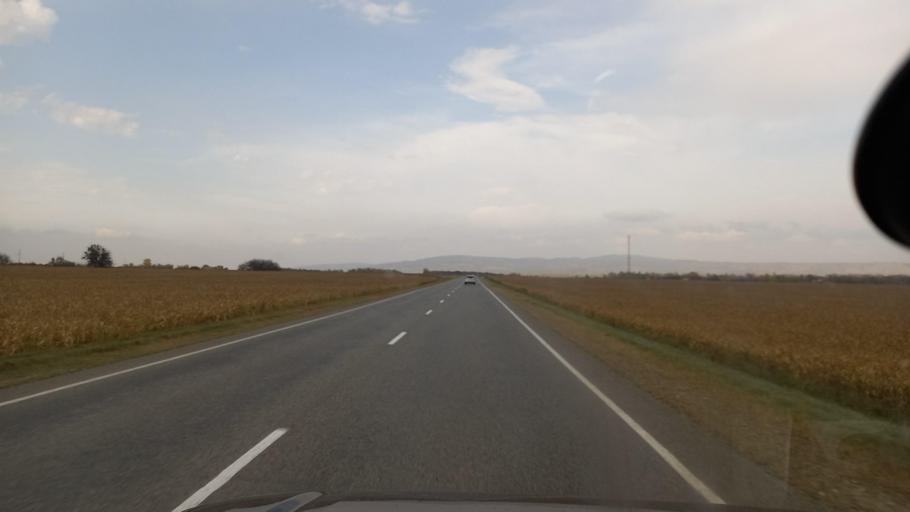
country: RU
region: Krasnodarskiy
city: Shedok
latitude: 44.2591
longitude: 40.8673
